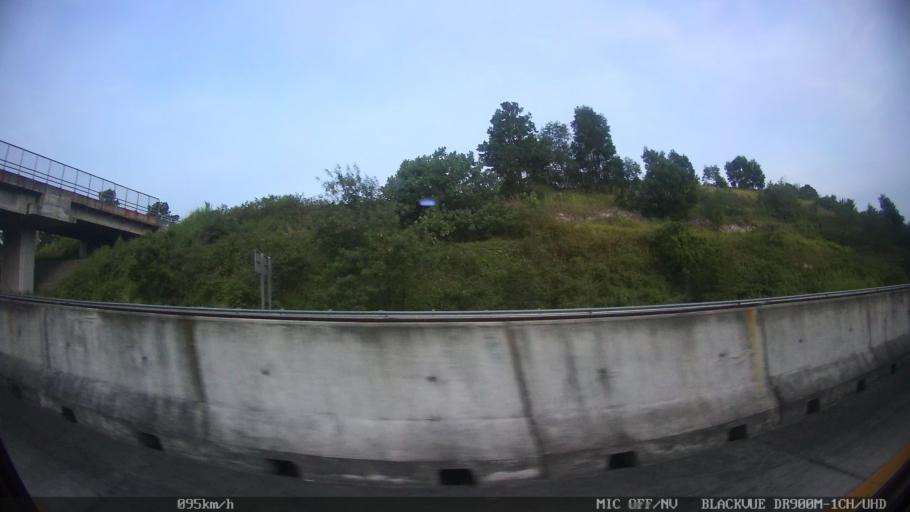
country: ID
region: Lampung
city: Penengahan
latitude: -5.8209
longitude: 105.7361
